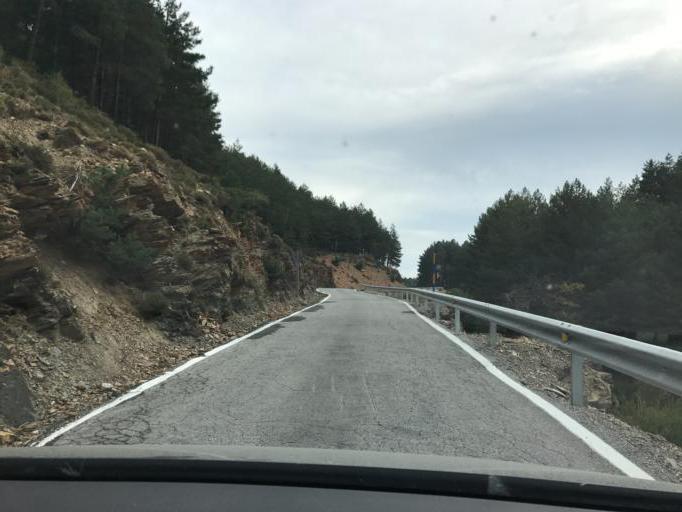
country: ES
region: Andalusia
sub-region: Provincia de Granada
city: Ferreira
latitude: 37.1194
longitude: -3.0327
